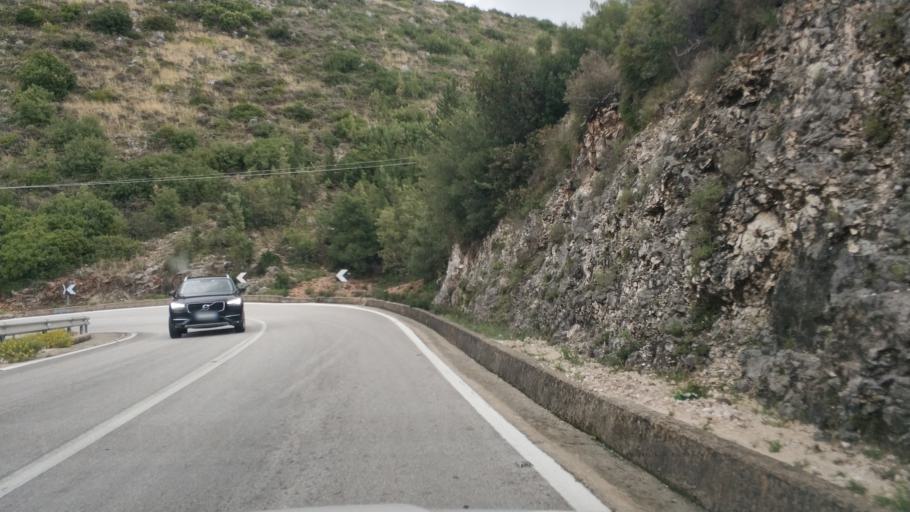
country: AL
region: Vlore
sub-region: Rrethi i Vlores
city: Vranisht
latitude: 40.1432
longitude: 19.6619
